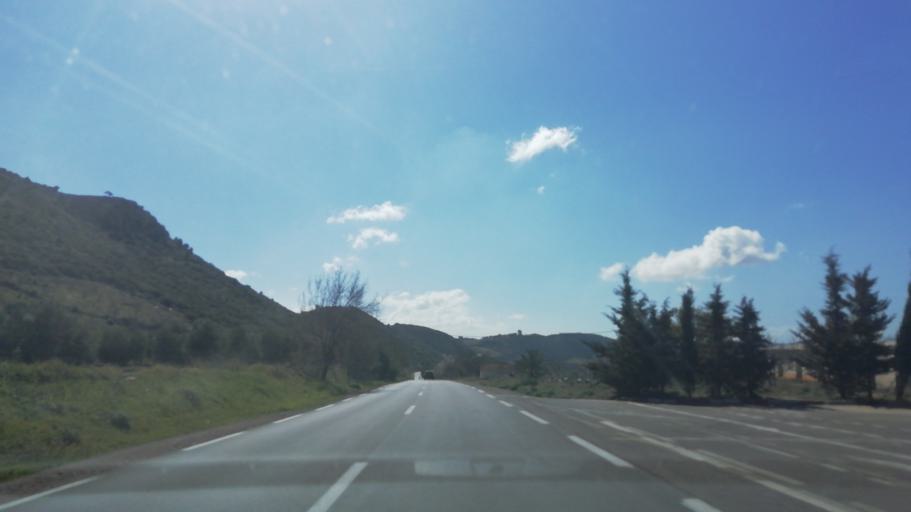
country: DZ
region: Mascara
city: Mascara
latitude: 35.4737
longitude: 0.1566
